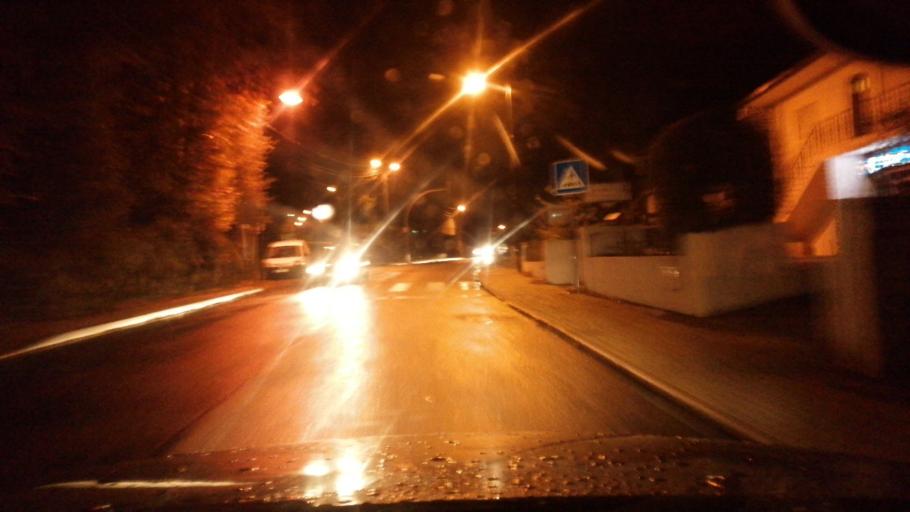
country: PT
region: Viseu
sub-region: Moimenta da Beira
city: Moimenta da Beira
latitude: 40.9460
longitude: -7.5735
